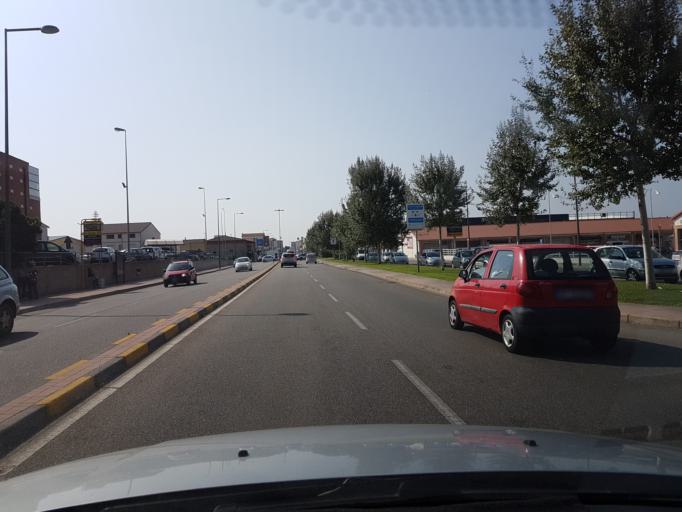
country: IT
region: Sardinia
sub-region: Provincia di Oristano
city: Oristano
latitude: 39.9159
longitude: 8.5850
